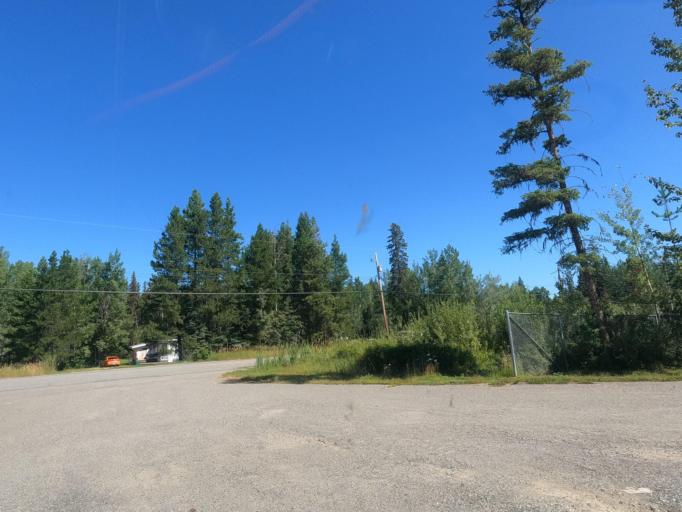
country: CA
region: British Columbia
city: Quesnel
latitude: 53.0208
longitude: -122.4545
